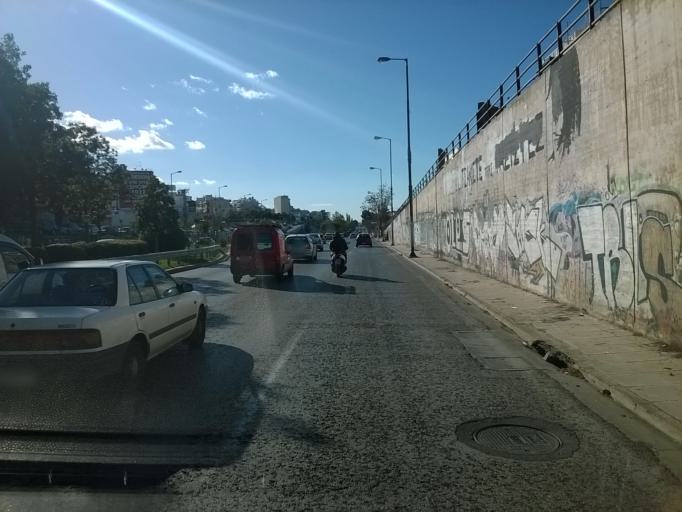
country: GR
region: Attica
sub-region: Nomarchia Athinas
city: Agios Dimitrios
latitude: 37.9318
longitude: 23.7443
